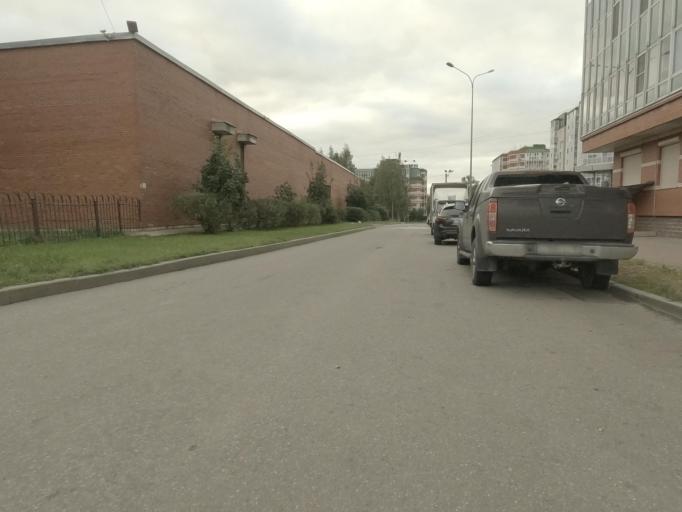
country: RU
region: St.-Petersburg
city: Krasnogvargeisky
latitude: 59.9637
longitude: 30.4922
